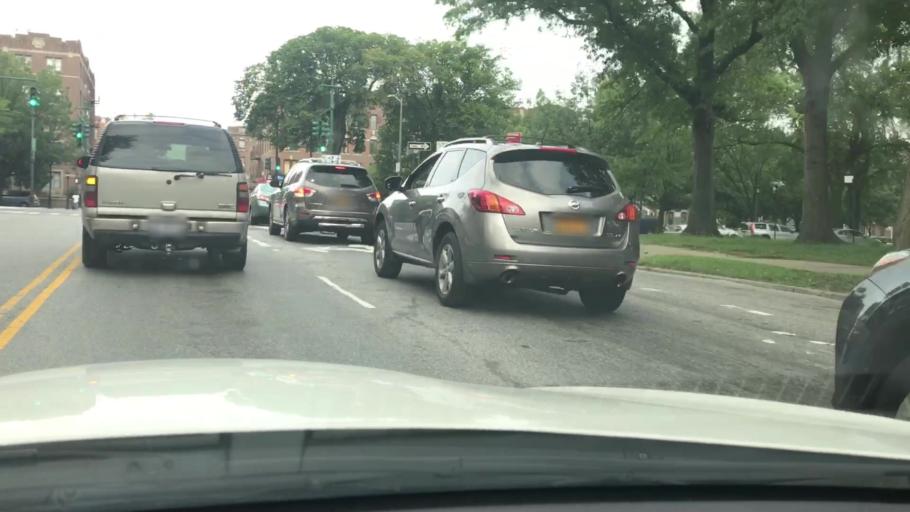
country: US
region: New York
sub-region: Kings County
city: Brooklyn
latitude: 40.6679
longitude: -73.9257
